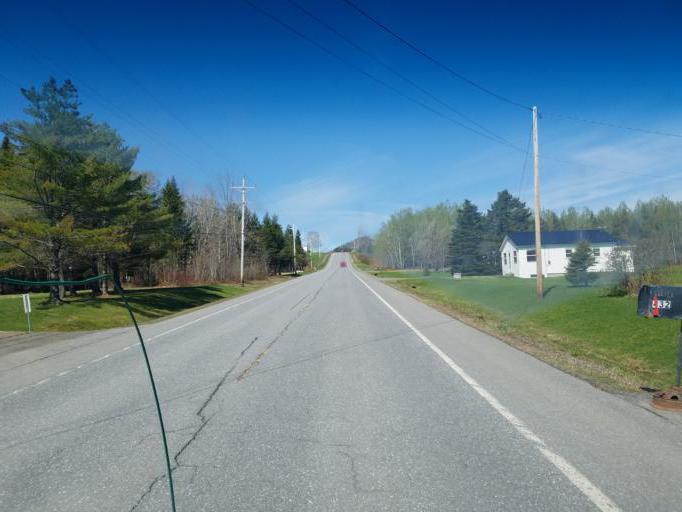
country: US
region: Maine
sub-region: Aroostook County
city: Presque Isle
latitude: 46.6668
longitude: -68.2063
